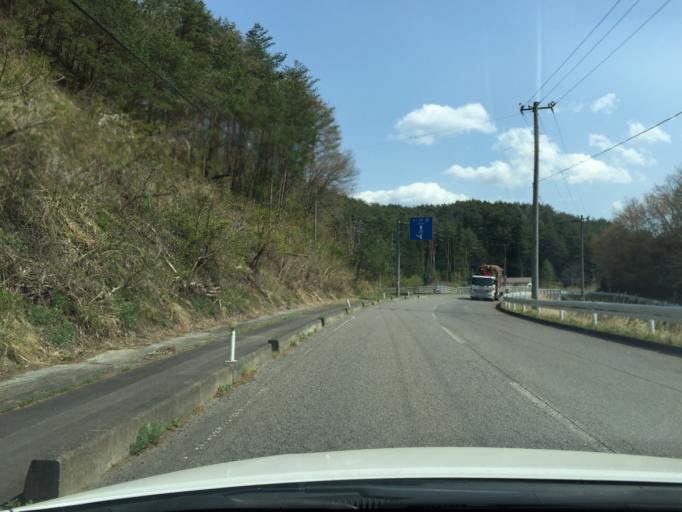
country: JP
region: Fukushima
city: Namie
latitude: 37.4135
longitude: 140.7957
